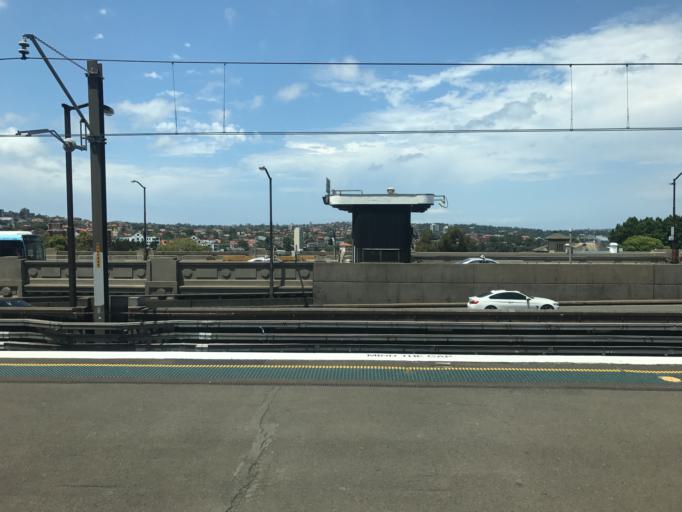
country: AU
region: New South Wales
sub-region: North Sydney
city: Milsons Point
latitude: -33.8463
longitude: 151.2120
